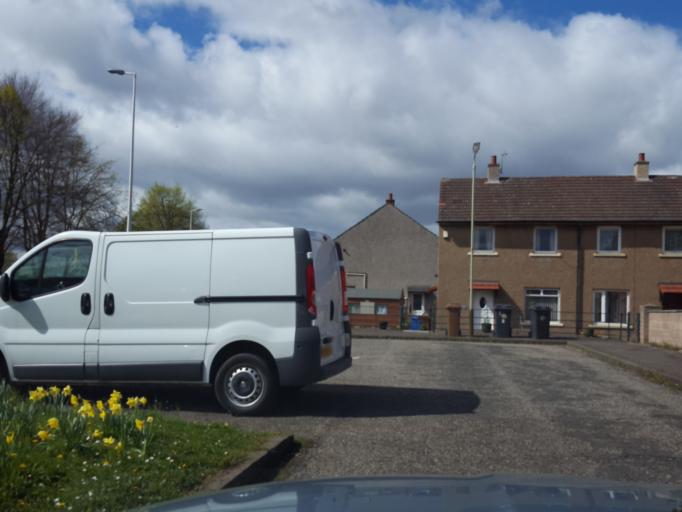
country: GB
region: Scotland
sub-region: Angus
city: Muirhead
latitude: 56.4717
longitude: -3.0472
